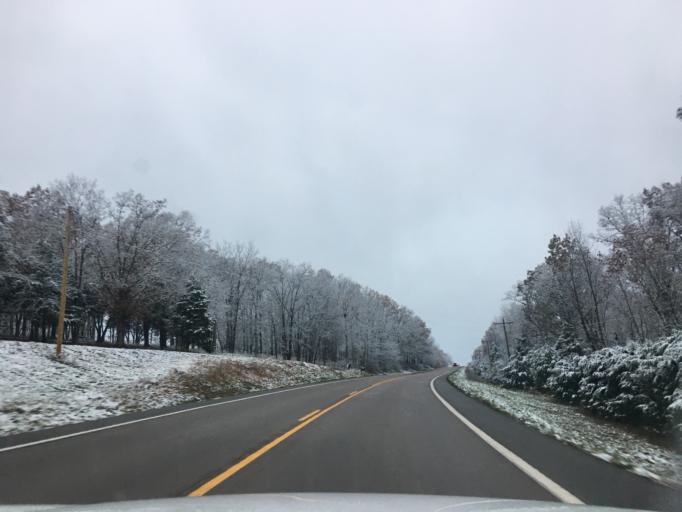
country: US
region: Missouri
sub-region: Osage County
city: Linn
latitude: 38.4698
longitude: -91.7775
